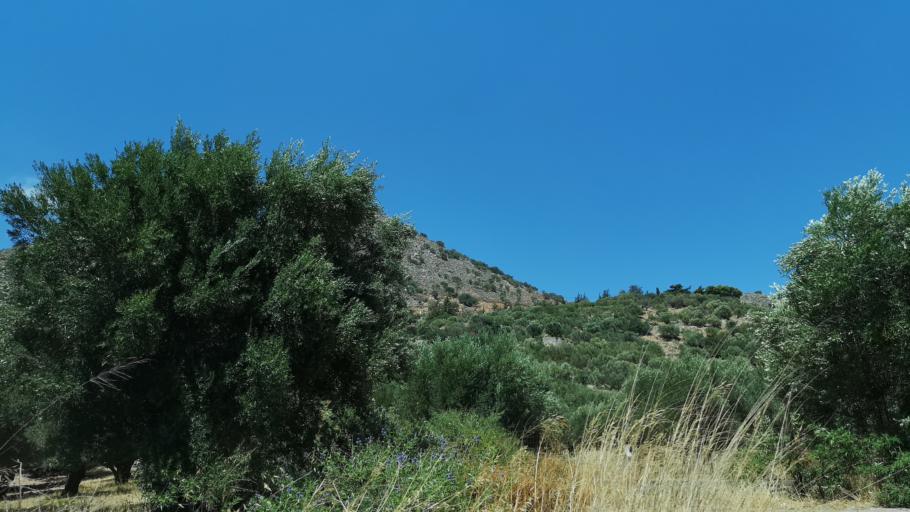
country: GR
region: Crete
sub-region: Nomos Lasithiou
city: Neapoli
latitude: 35.2483
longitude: 25.6257
